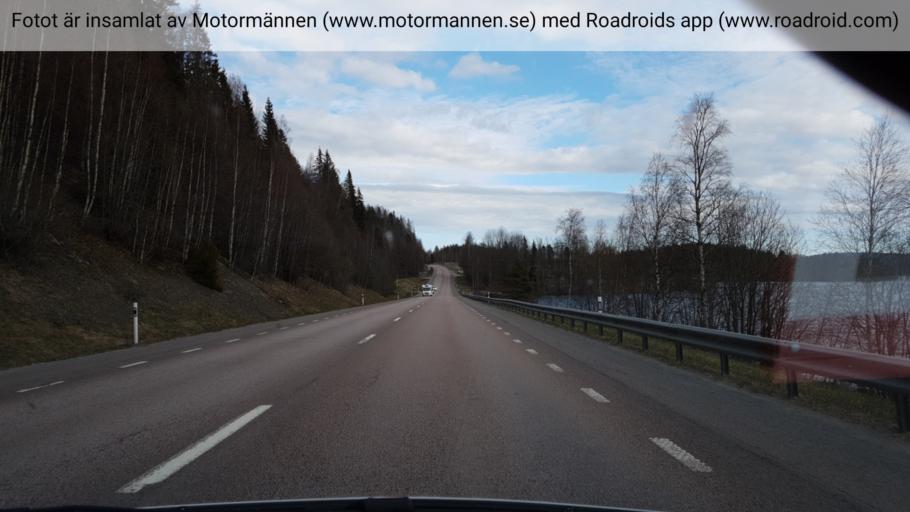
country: SE
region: Vaesternorrland
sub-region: Kramfors Kommun
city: Kramfors
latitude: 62.7978
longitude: 17.8775
